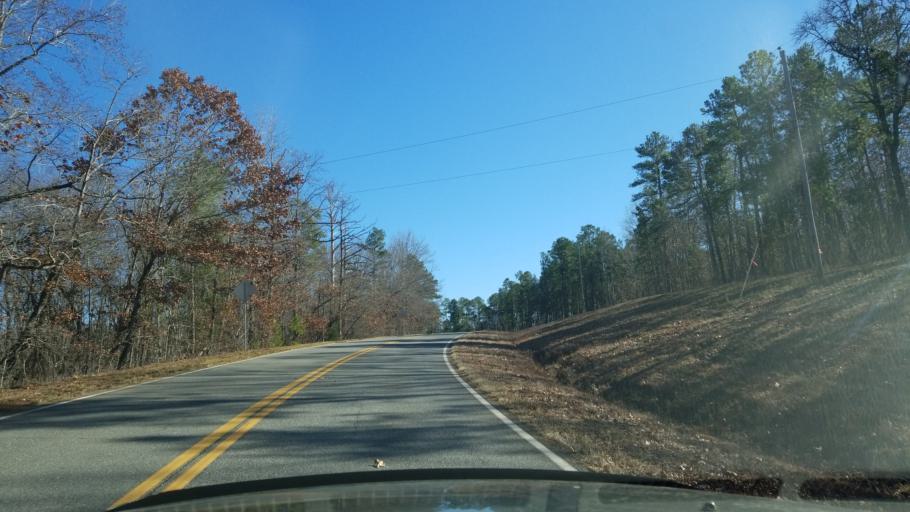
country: US
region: Georgia
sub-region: Meriwether County
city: Manchester
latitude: 32.8433
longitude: -84.6755
